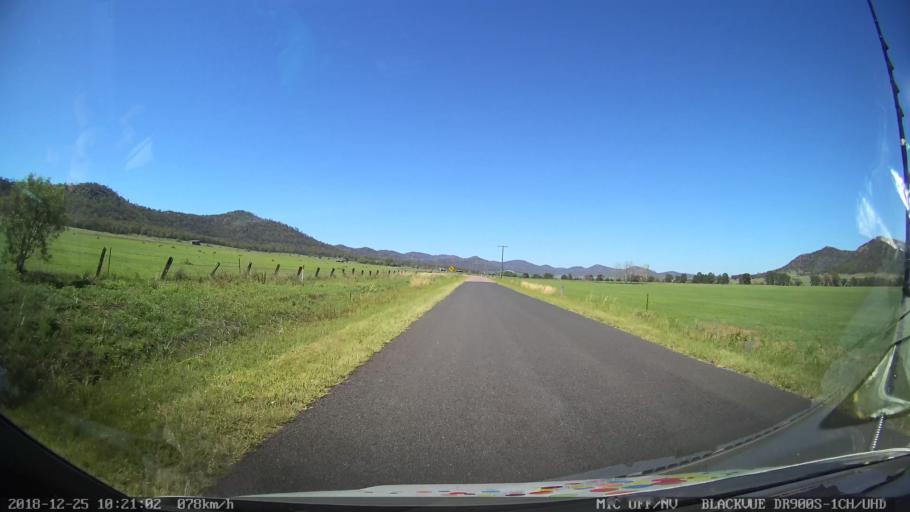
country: AU
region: New South Wales
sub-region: Muswellbrook
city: Denman
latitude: -32.3632
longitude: 150.5438
